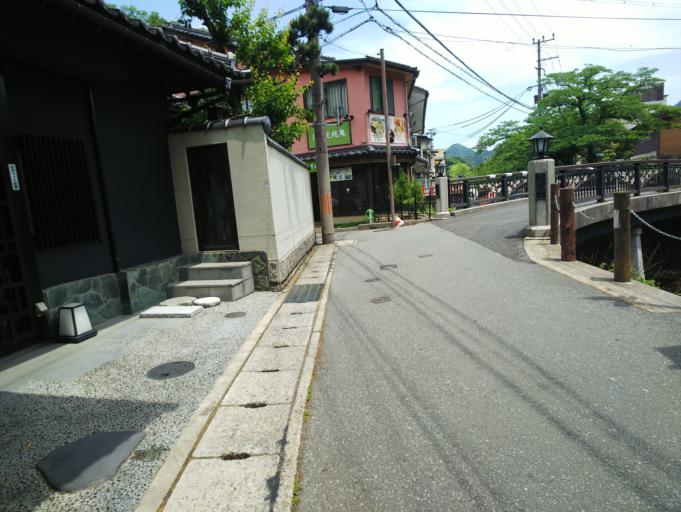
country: JP
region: Hyogo
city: Toyooka
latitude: 35.6257
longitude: 134.8088
